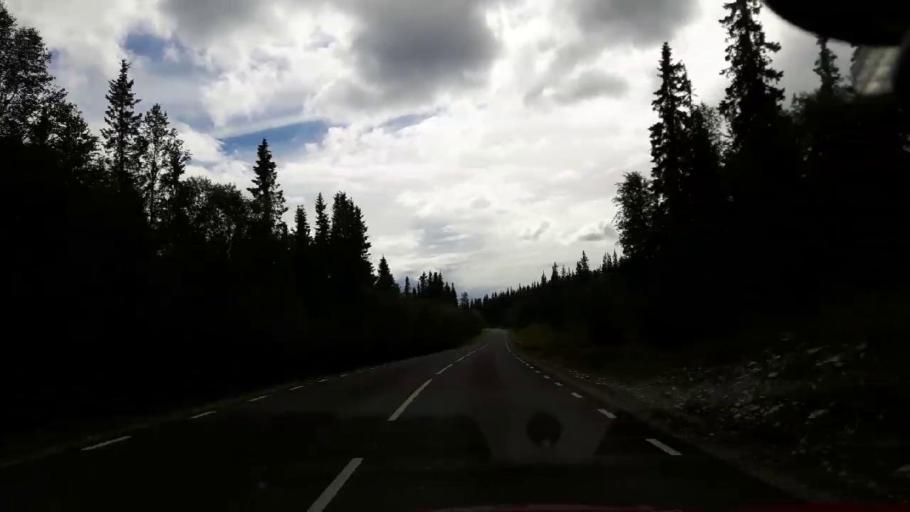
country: NO
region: Nord-Trondelag
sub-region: Royrvik
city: Royrvik
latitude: 64.8120
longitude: 14.0658
